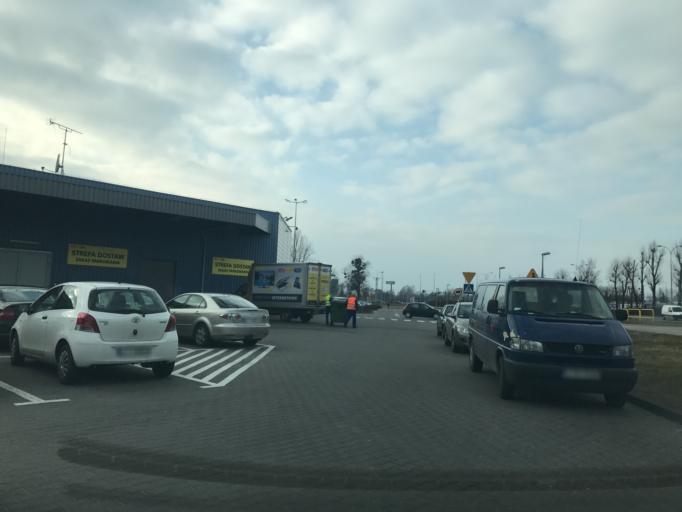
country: PL
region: Kujawsko-Pomorskie
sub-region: Powiat torunski
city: Lubicz Dolny
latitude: 53.0334
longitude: 18.6948
